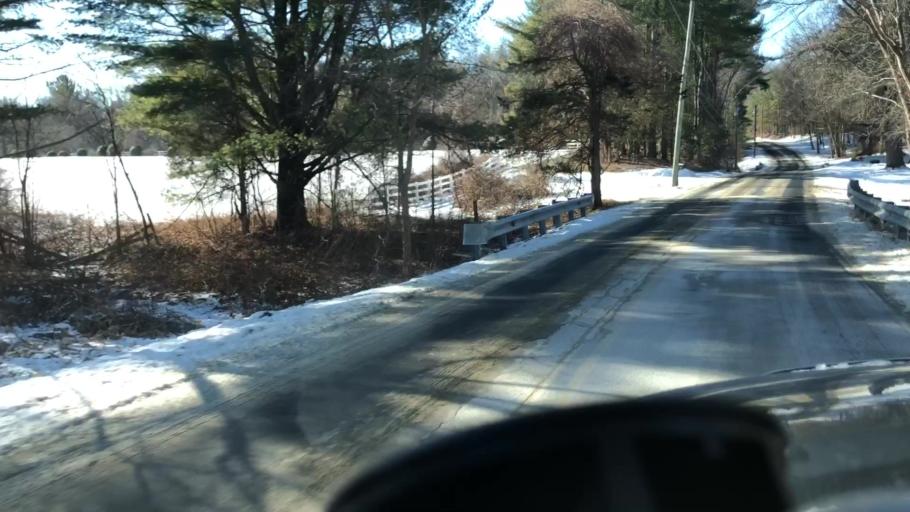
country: US
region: Massachusetts
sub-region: Hampshire County
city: Southampton
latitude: 42.2240
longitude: -72.7099
